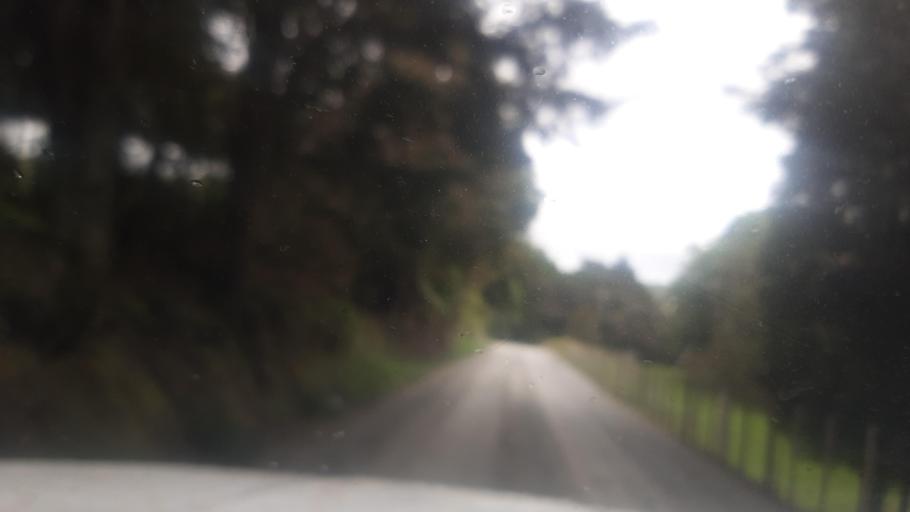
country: NZ
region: Northland
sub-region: Far North District
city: Taipa
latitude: -35.0989
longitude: 173.3979
